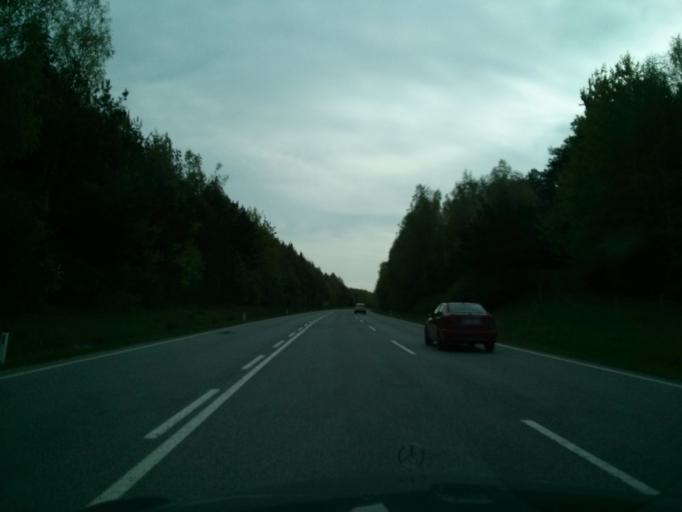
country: AT
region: Burgenland
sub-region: Politischer Bezirk Oberwart
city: Markt Allhau
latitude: 47.2783
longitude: 16.0983
